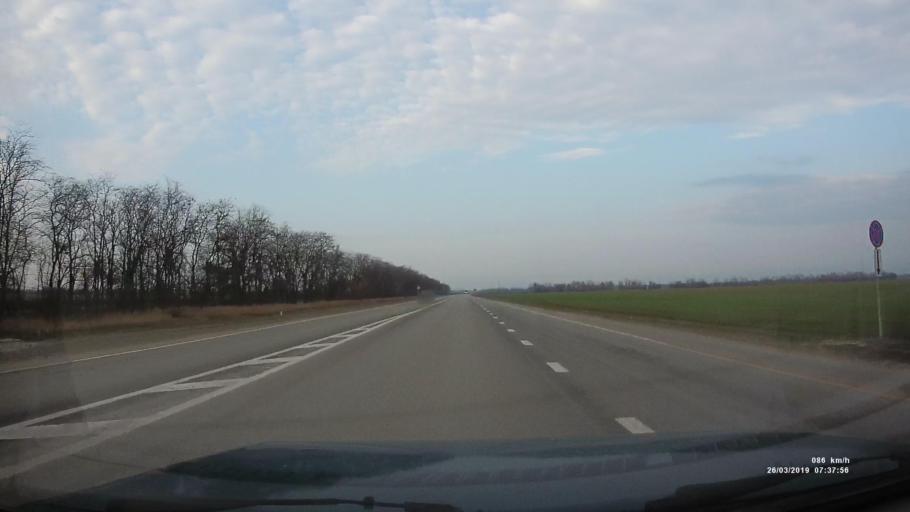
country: RU
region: Rostov
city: Novobessergenovka
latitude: 47.2007
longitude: 38.6924
